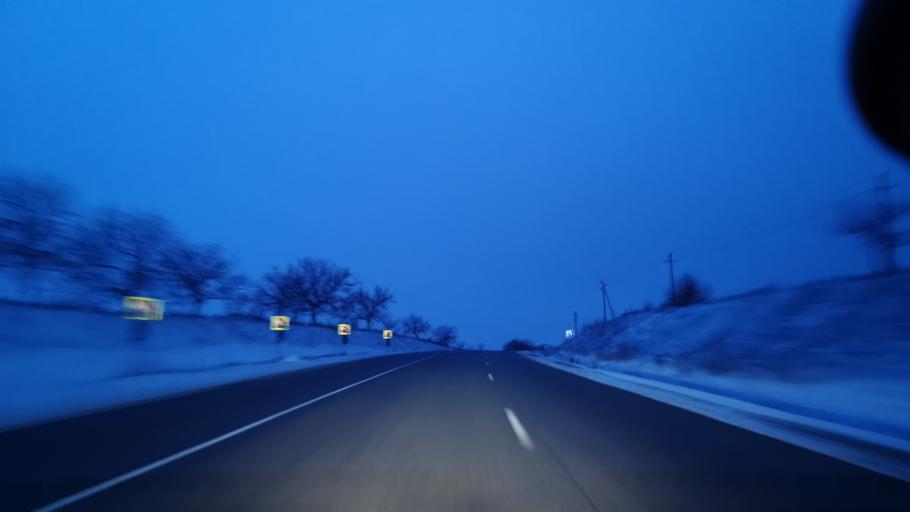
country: MD
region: Rezina
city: Saharna
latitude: 47.5856
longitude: 28.8177
